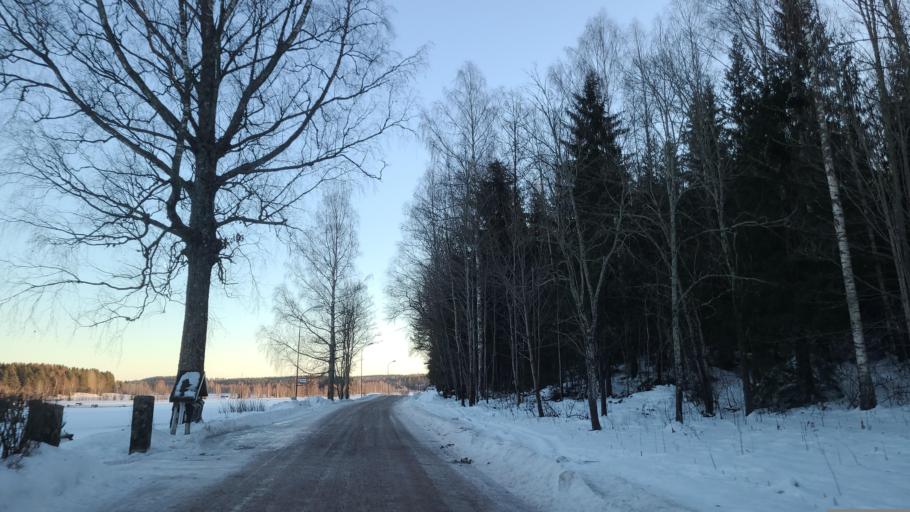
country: SE
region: Gaevleborg
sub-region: Soderhamns Kommun
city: Soderhamn
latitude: 61.2779
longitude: 16.9851
